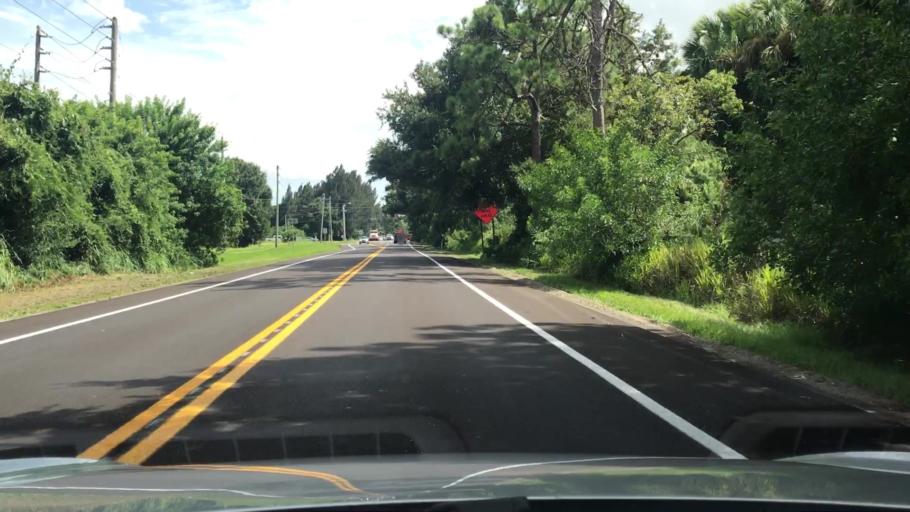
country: US
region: Florida
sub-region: Indian River County
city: Winter Beach
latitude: 27.7506
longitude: -80.4620
